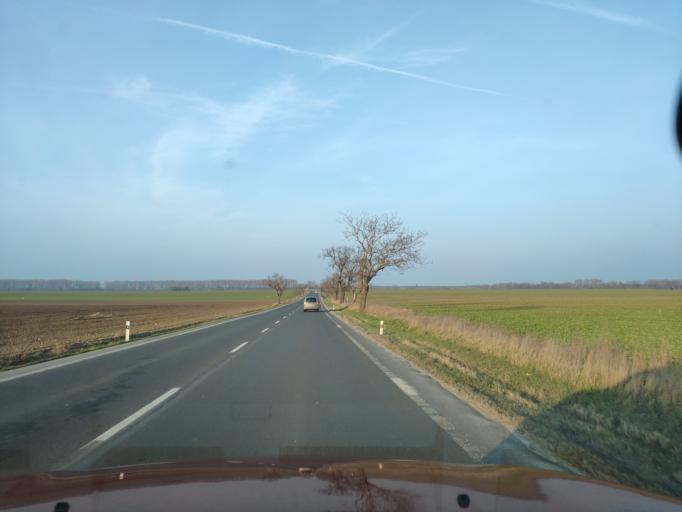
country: SK
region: Trnavsky
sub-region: Okres Trnava
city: Trnava
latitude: 48.3172
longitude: 17.5088
